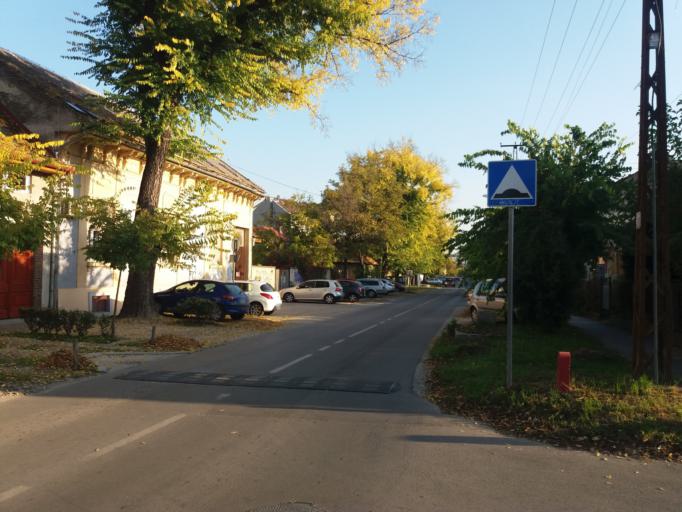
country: RS
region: Autonomna Pokrajina Vojvodina
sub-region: Severnobacki Okrug
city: Subotica
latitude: 46.0956
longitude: 19.6638
